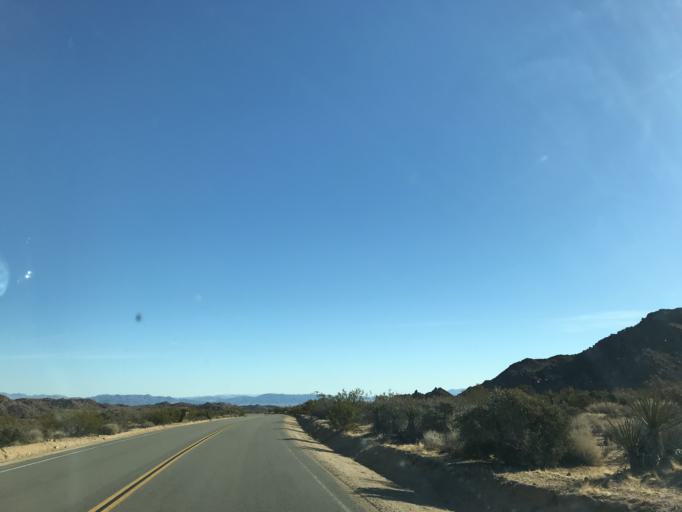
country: US
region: California
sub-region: Riverside County
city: Mecca
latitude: 33.7852
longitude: -115.7953
